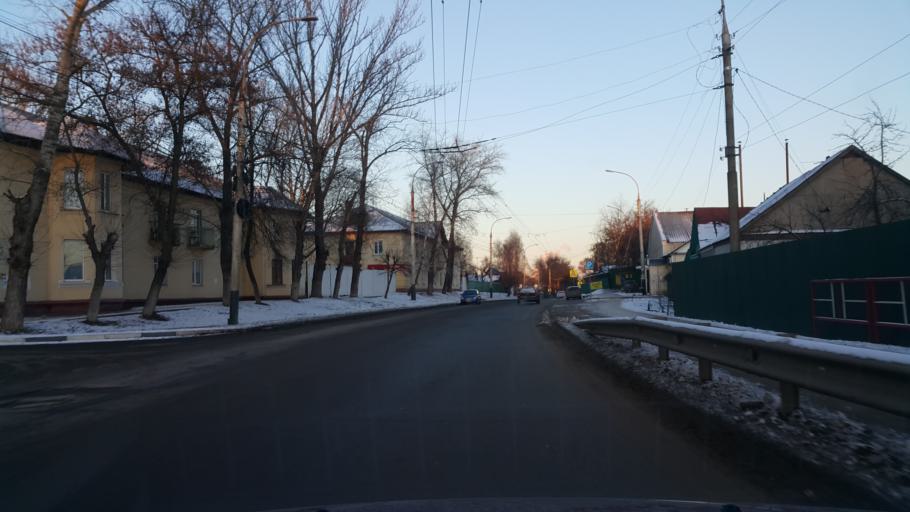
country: RU
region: Tambov
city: Pokrovo-Prigorodnoye
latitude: 52.7125
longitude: 41.4008
